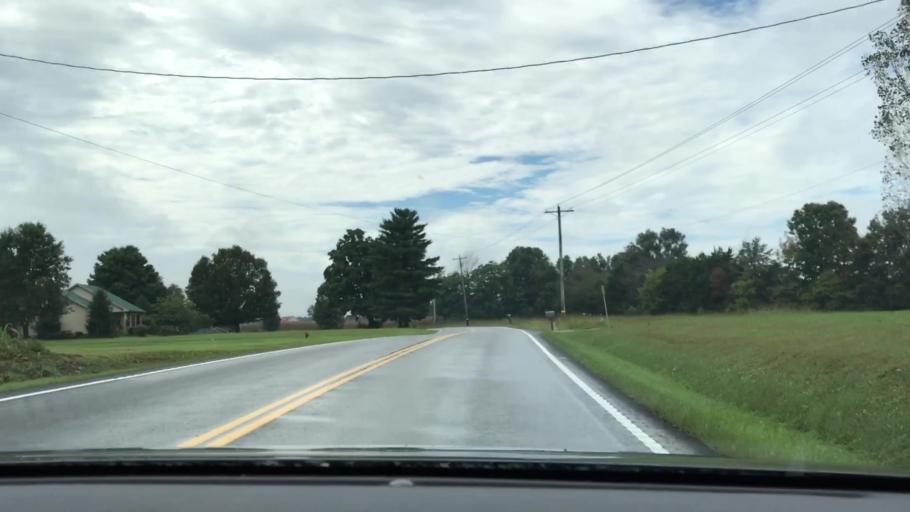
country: US
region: Tennessee
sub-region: Macon County
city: Red Boiling Springs
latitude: 36.5063
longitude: -85.8632
